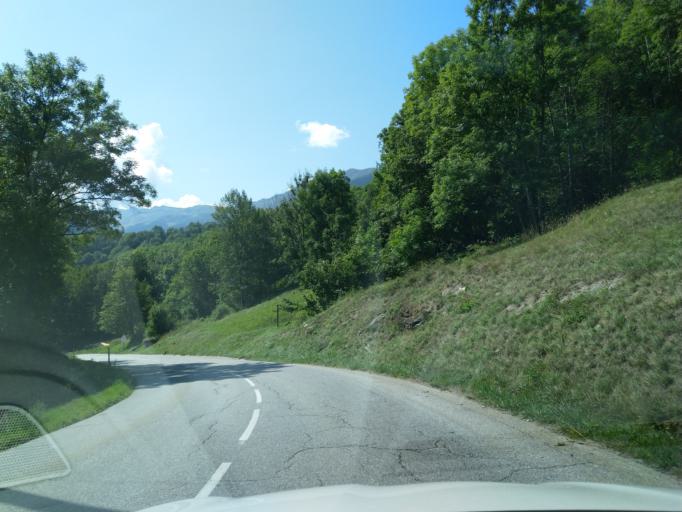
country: FR
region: Rhone-Alpes
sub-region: Departement de la Savoie
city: Les Allues
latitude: 45.4415
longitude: 6.5572
